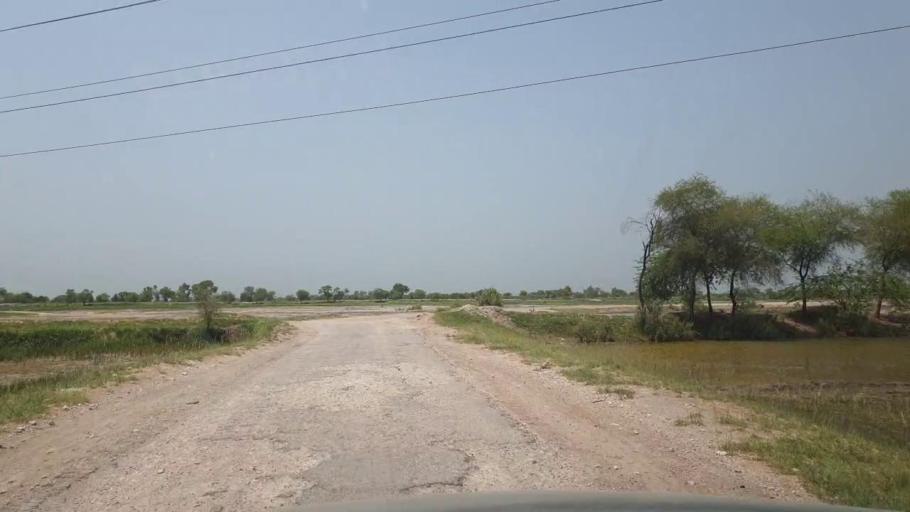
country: PK
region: Sindh
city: Garhi Yasin
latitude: 27.8731
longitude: 68.4471
